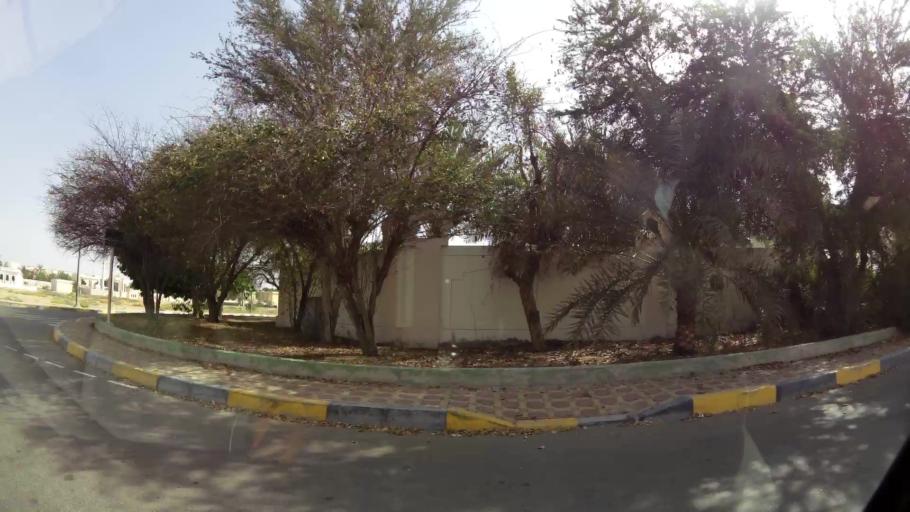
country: AE
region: Abu Dhabi
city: Al Ain
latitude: 24.2465
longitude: 55.6920
